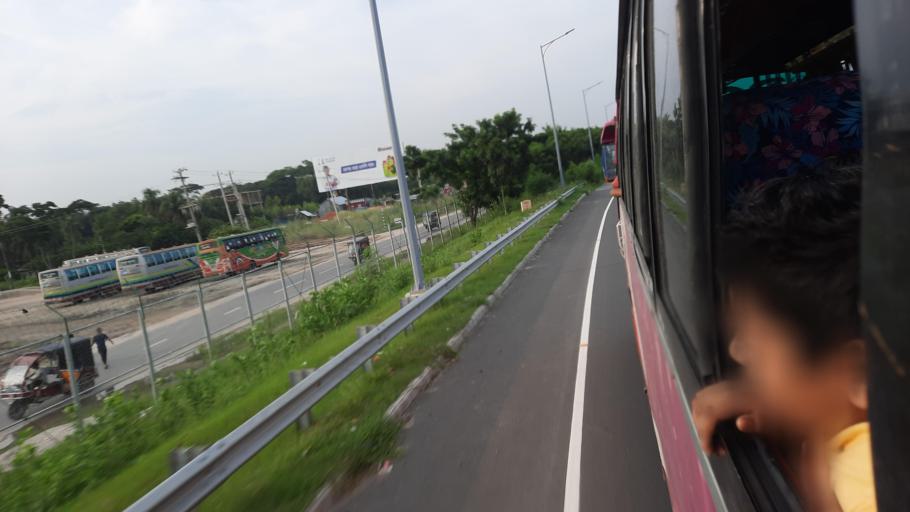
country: BD
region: Dhaka
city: Dohar
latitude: 23.4799
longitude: 90.2669
